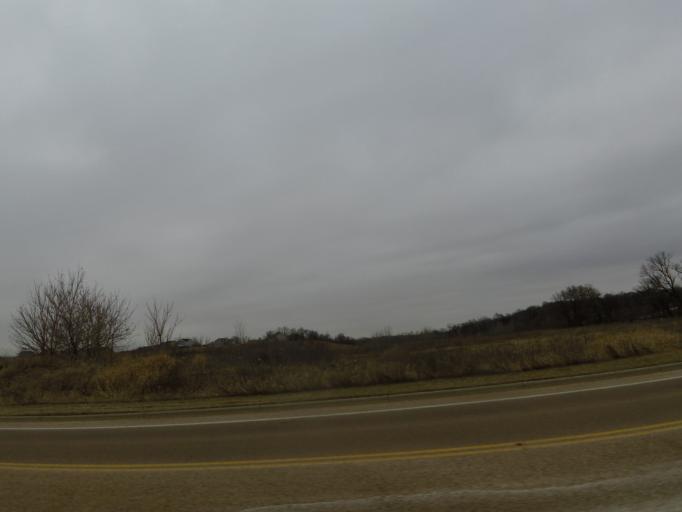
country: US
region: Minnesota
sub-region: Carver County
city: Watertown
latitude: 44.9631
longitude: -93.8271
